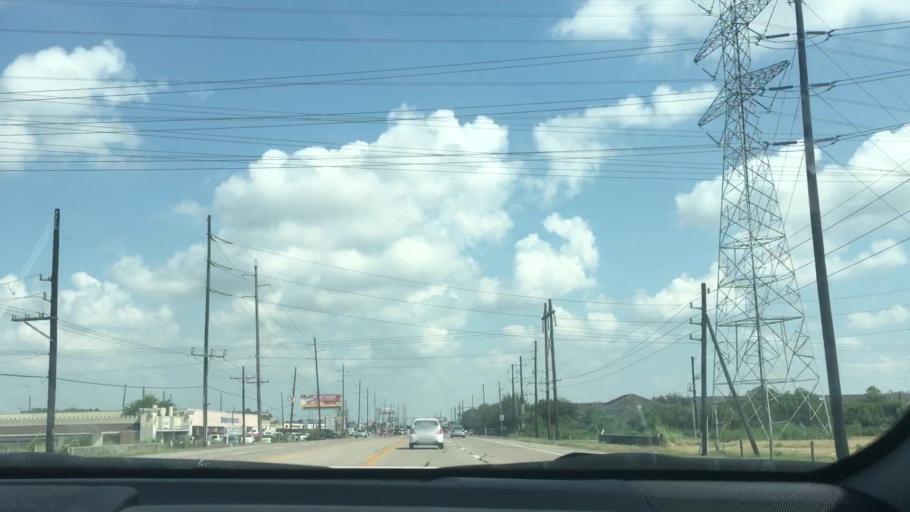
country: US
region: Texas
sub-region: Fort Bend County
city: Stafford
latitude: 29.6049
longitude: -95.5644
